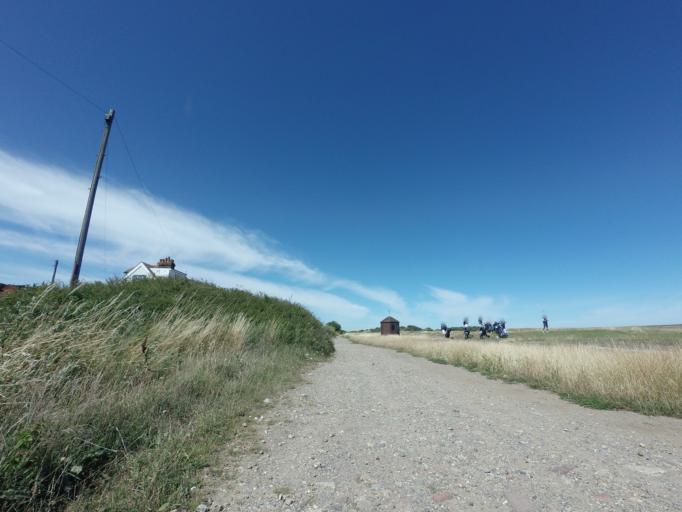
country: GB
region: England
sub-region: Kent
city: Deal
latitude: 51.2409
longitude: 1.3965
